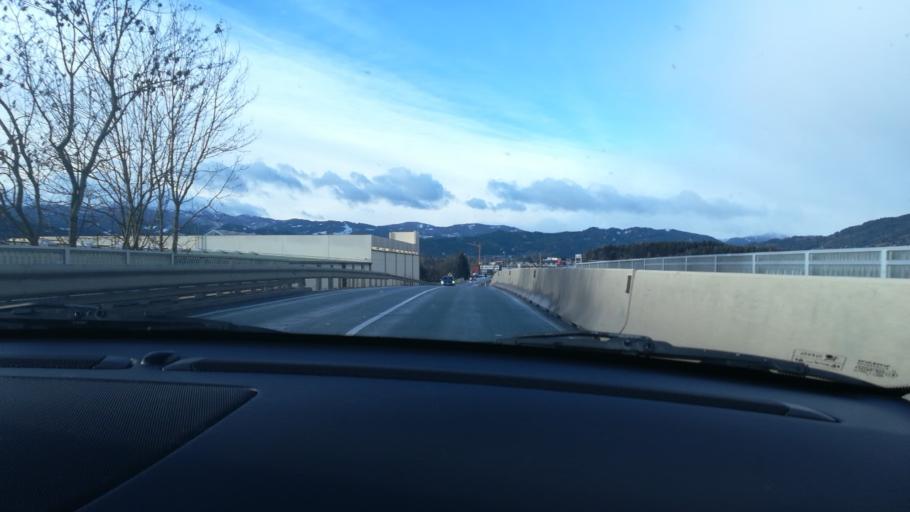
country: AT
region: Styria
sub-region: Politischer Bezirk Murtal
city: Zeltweg
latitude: 47.1951
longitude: 14.7276
